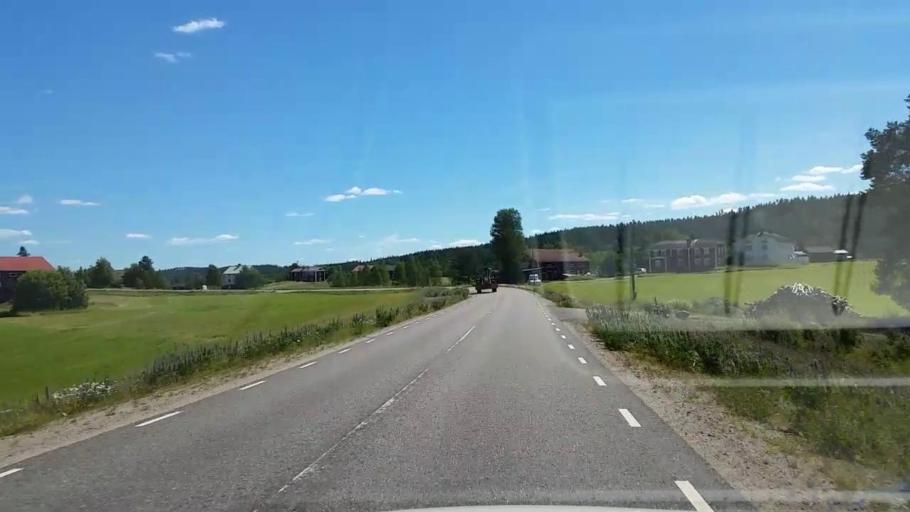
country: SE
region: Gaevleborg
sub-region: Ovanakers Kommun
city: Edsbyn
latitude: 61.4219
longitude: 15.7343
